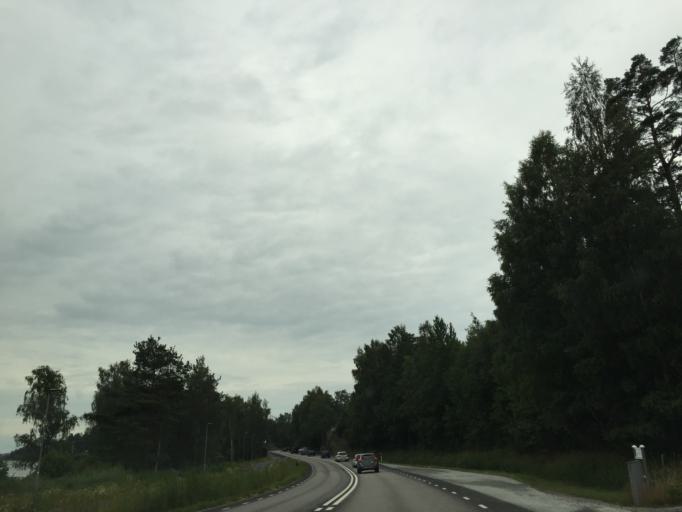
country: SE
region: Vaestra Goetaland
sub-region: Tjorns Kommun
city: Myggenas
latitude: 58.0534
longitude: 11.7570
